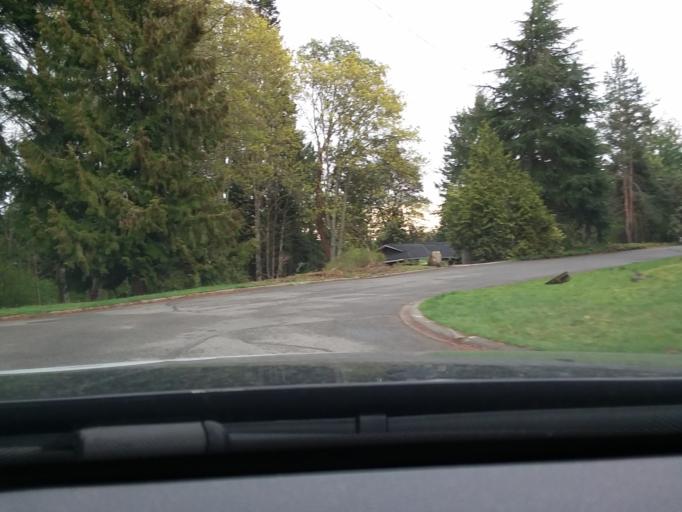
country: CA
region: British Columbia
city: North Saanich
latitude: 48.6185
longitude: -123.4258
